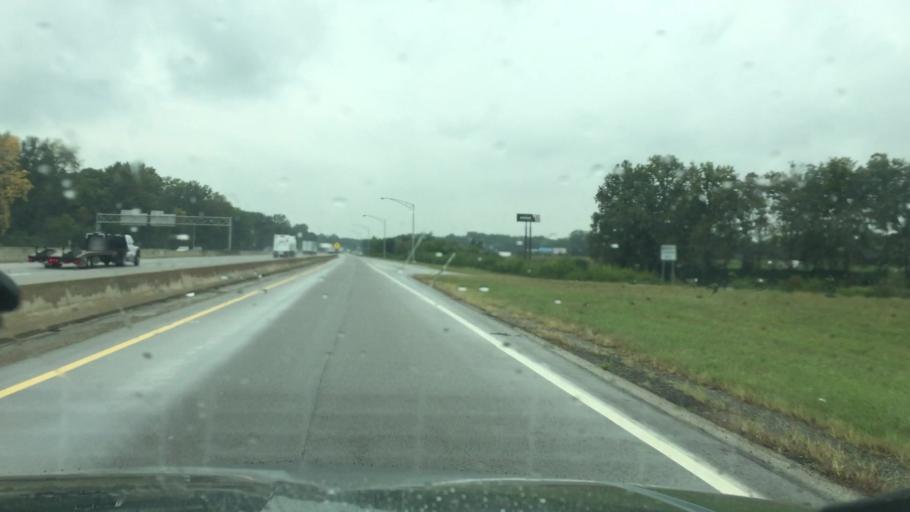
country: US
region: Ohio
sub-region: Clark County
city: Holiday Valley
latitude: 39.8652
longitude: -83.9978
